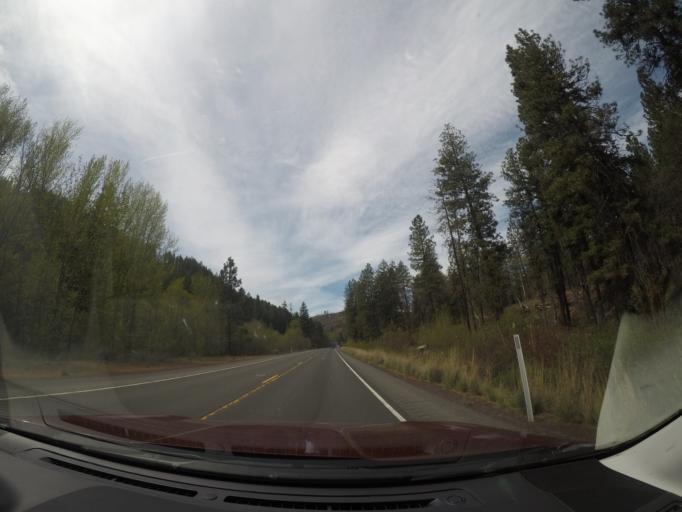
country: US
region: Washington
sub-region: Klickitat County
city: Goldendale
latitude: 46.0277
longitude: -120.6173
